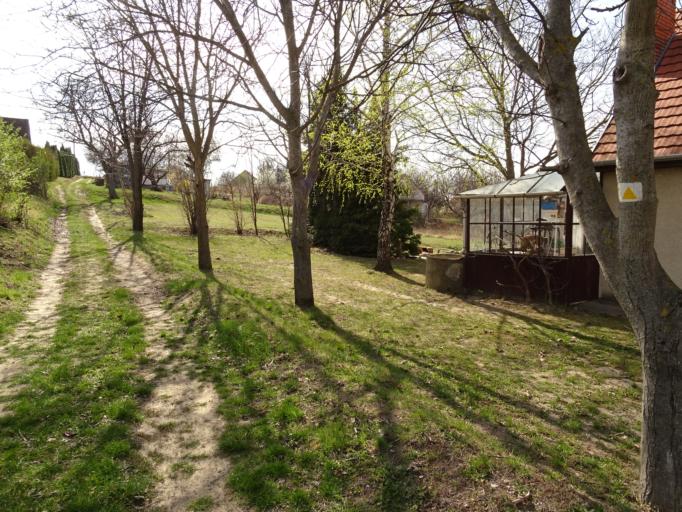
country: HU
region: Fejer
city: Lovasbereny
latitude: 47.3024
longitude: 18.5746
